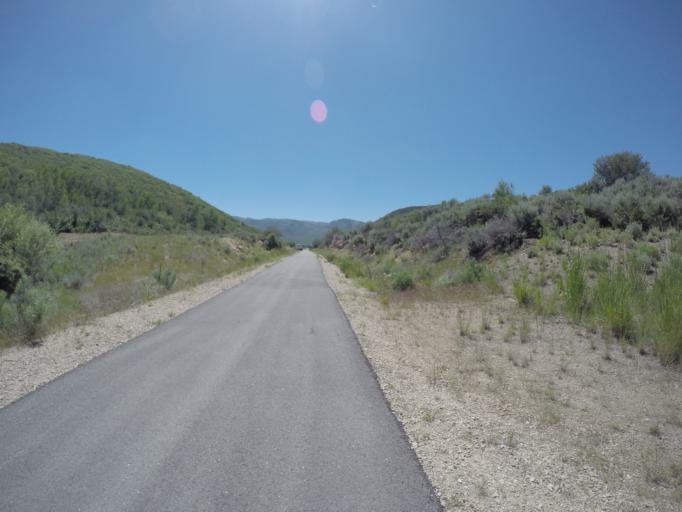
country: US
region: Utah
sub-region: Summit County
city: Park City
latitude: 40.6713
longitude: -111.4720
